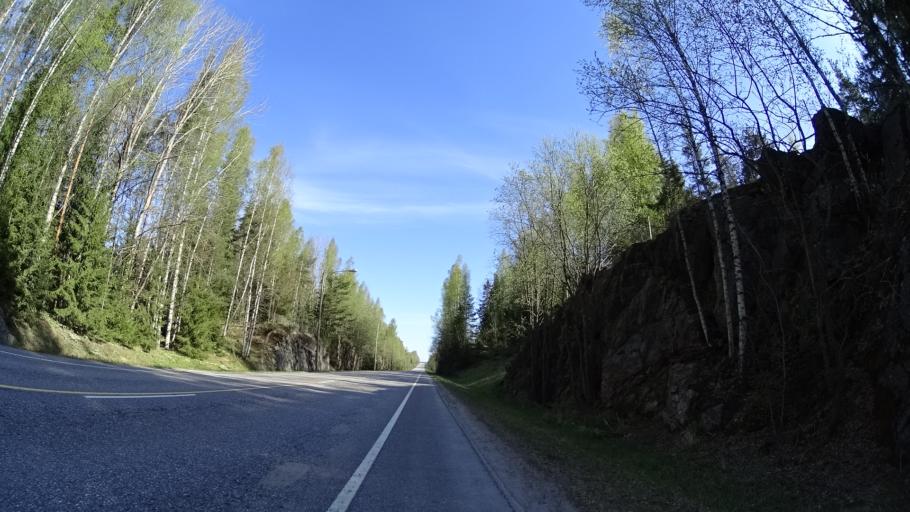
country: FI
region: Uusimaa
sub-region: Helsinki
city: Nurmijaervi
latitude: 60.3747
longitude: 24.8059
